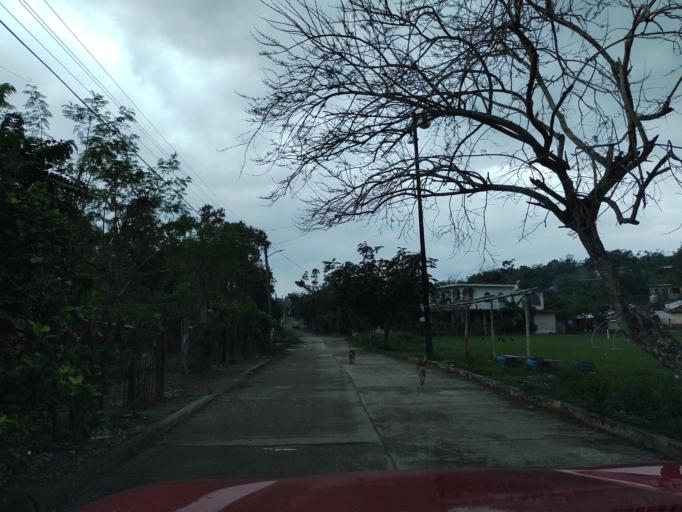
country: MX
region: Veracruz
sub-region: Papantla
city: El Chote
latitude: 20.4301
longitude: -97.3835
